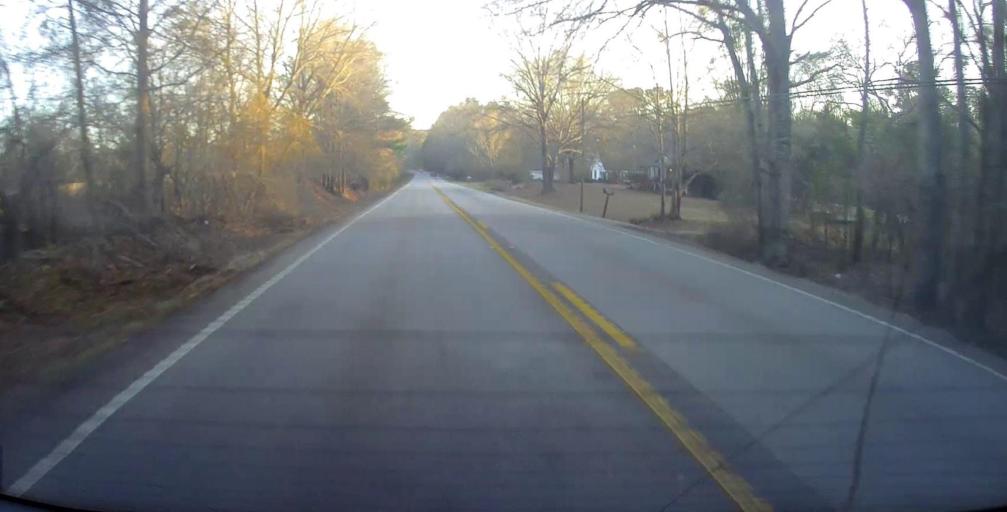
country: US
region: Georgia
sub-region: Troup County
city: La Grange
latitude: 32.9772
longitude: -85.0275
